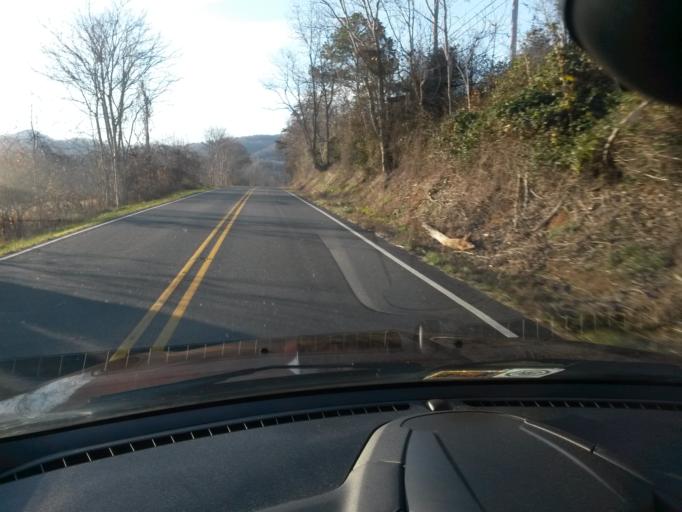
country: US
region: Virginia
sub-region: City of Buena Vista
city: Buena Vista
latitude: 37.6663
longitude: -79.2018
